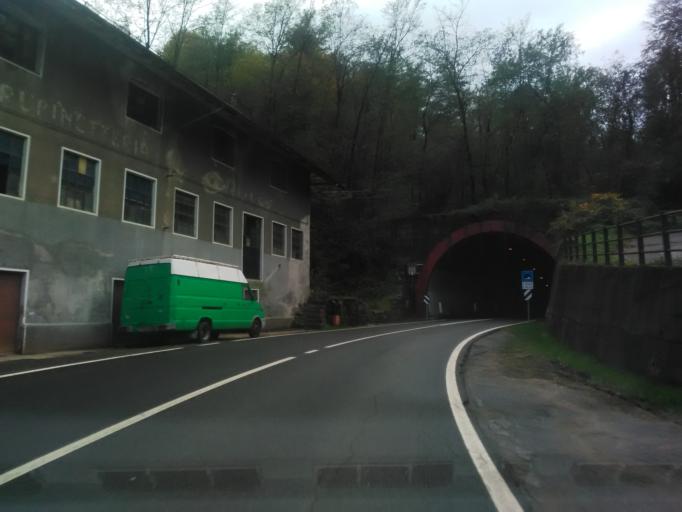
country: IT
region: Piedmont
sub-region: Provincia di Novara
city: Pogno
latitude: 45.7417
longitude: 8.3608
